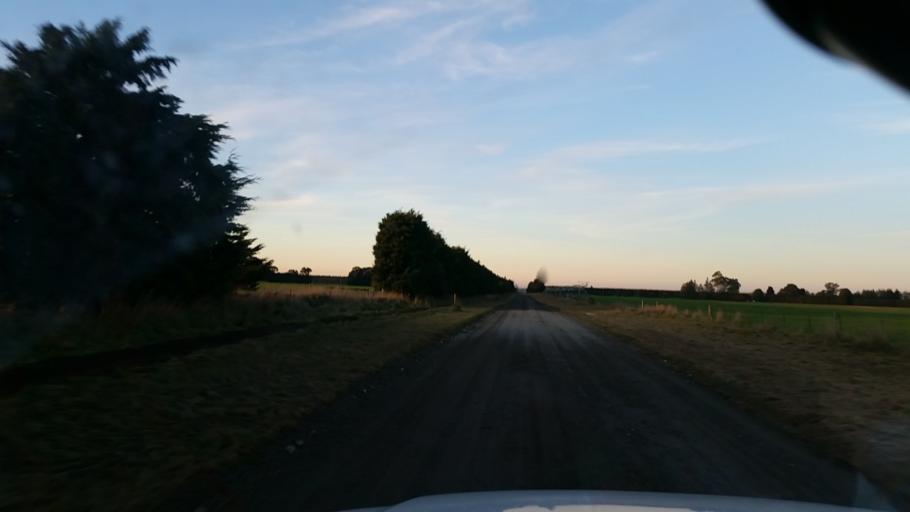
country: NZ
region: Canterbury
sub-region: Ashburton District
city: Methven
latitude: -43.7907
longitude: 171.5221
